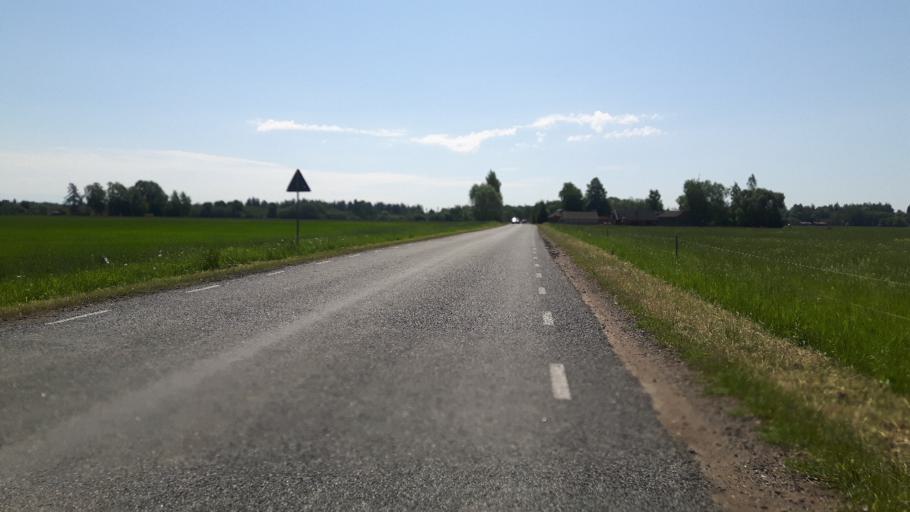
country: EE
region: Paernumaa
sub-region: Vaendra vald (alev)
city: Vandra
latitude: 58.5970
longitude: 25.0227
